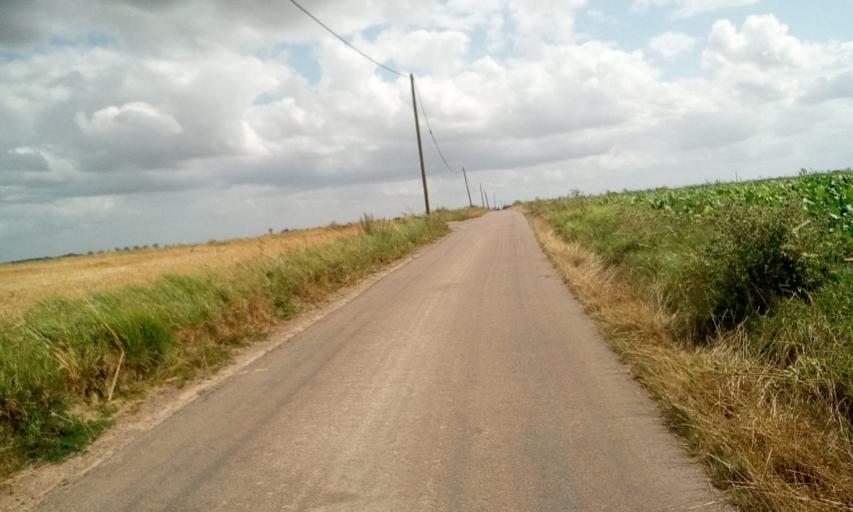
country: FR
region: Lower Normandy
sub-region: Departement du Calvados
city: Ver-sur-Mer
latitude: 49.3280
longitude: -0.5243
